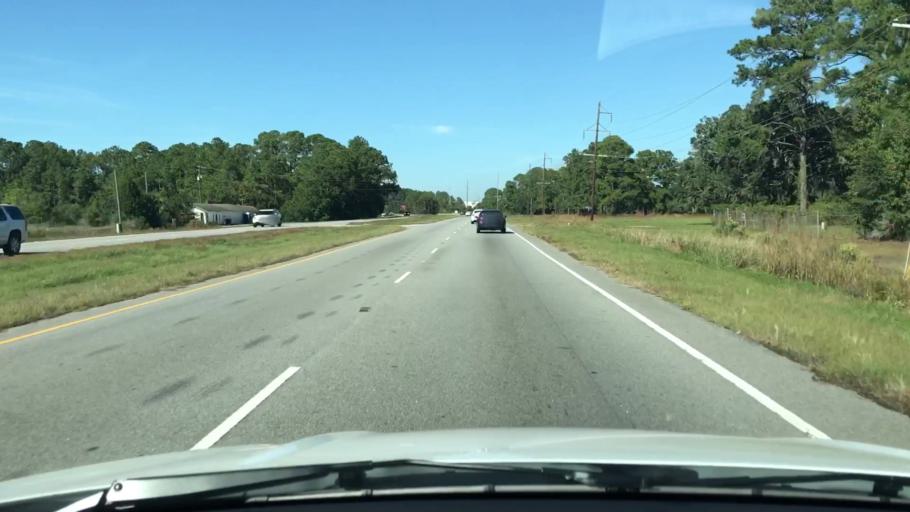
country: US
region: South Carolina
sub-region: Beaufort County
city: Laurel Bay
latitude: 32.5021
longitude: -80.7442
